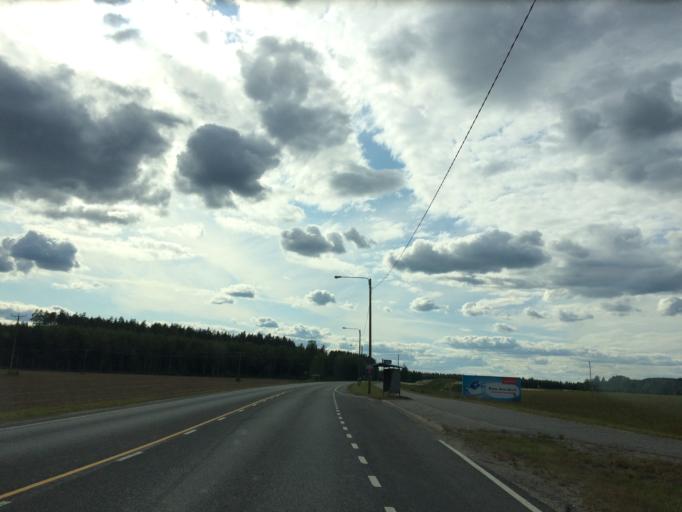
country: FI
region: Haeme
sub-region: Haemeenlinna
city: Turenki
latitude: 60.9207
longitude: 24.6127
